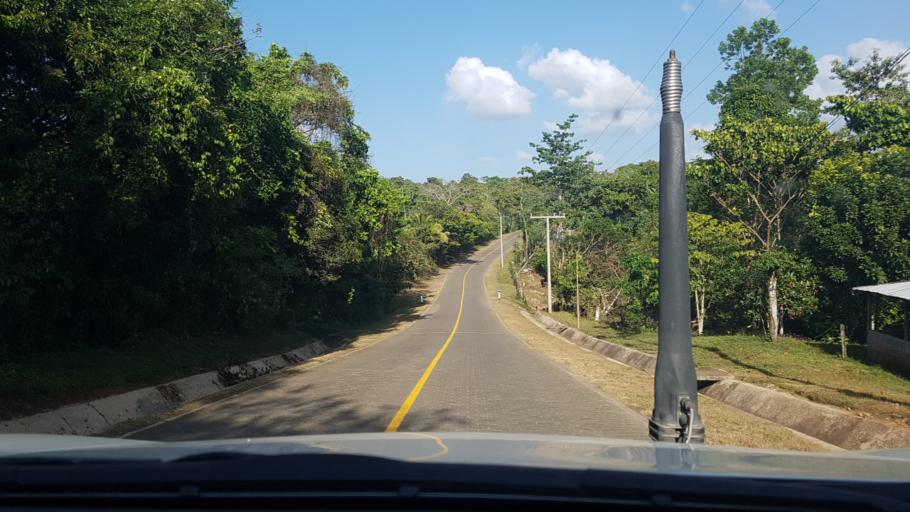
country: NI
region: Atlantico Sur
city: Nueva Guinea
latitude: 11.6880
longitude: -84.4324
